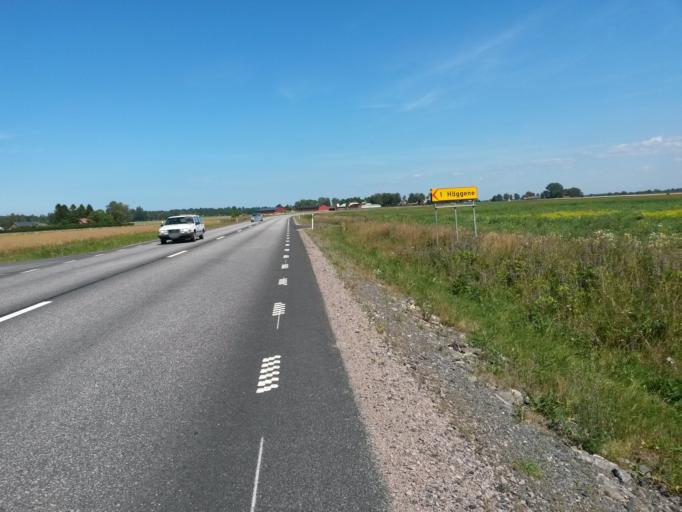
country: SE
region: Vaestra Goetaland
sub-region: Lidkopings Kommun
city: Lidkoping
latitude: 58.4768
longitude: 13.0765
